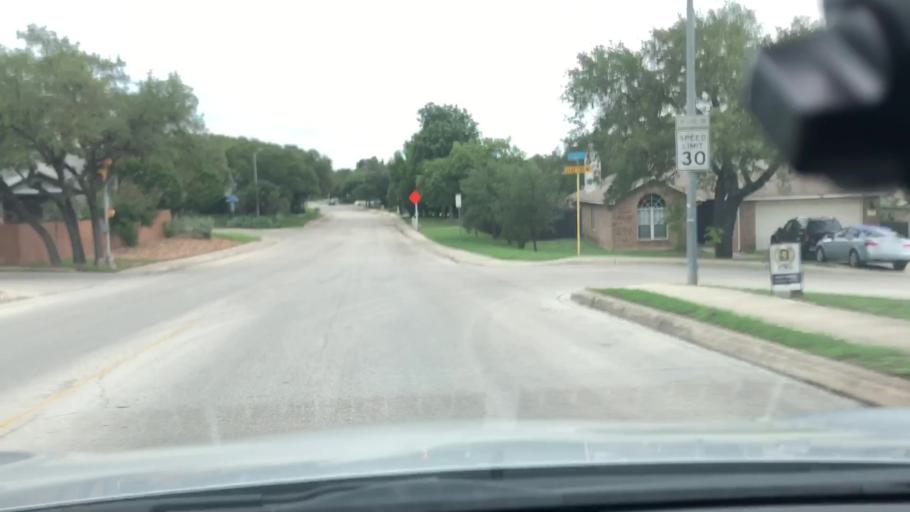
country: US
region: Texas
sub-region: Bexar County
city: Leon Valley
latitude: 29.5022
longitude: -98.6694
